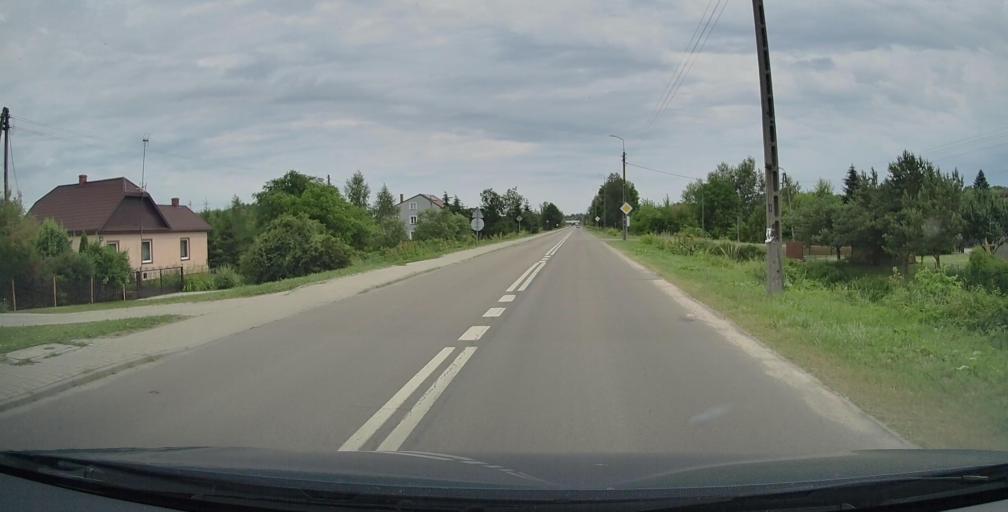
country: PL
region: Lublin Voivodeship
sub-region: Powiat bialski
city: Terespol
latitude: 52.0759
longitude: 23.6314
